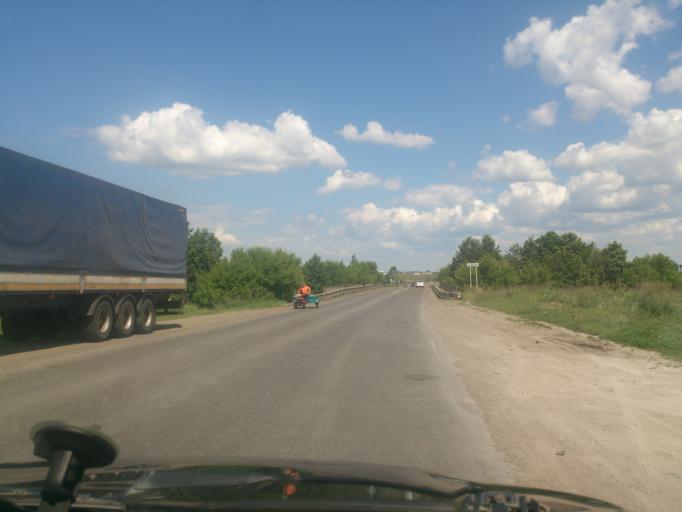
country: RU
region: Ulyanovsk
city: Cherdakly
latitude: 54.4320
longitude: 48.8997
